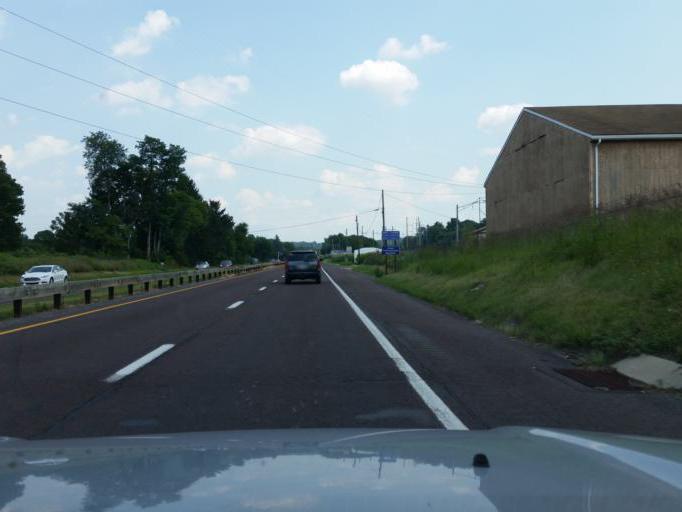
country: US
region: Pennsylvania
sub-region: Dauphin County
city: Hummelstown
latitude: 40.2604
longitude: -76.7215
